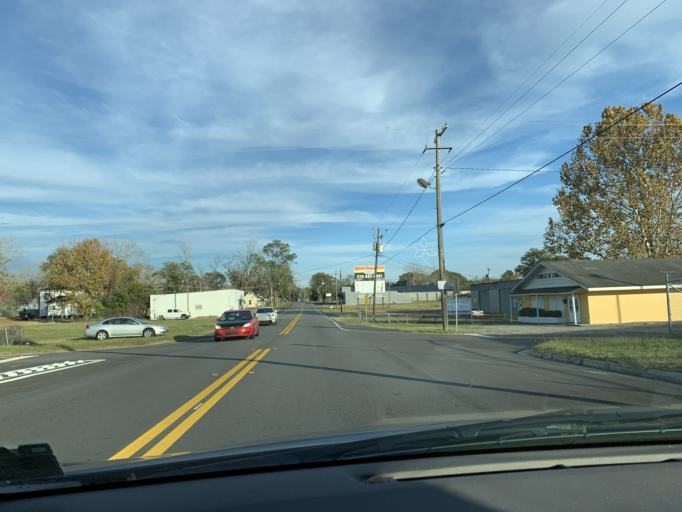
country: US
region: Georgia
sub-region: Irwin County
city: Ocilla
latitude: 31.5942
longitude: -83.2466
